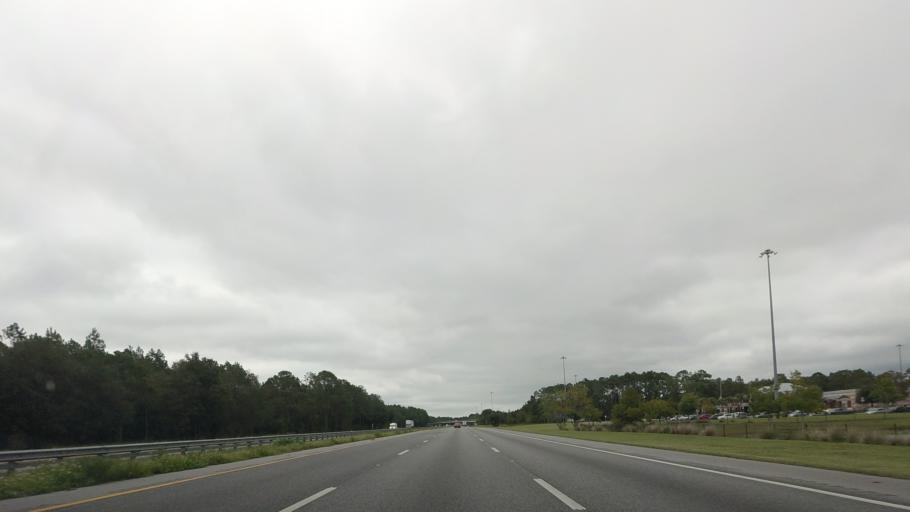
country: US
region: Georgia
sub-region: Echols County
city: Statenville
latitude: 30.6144
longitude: -83.1478
